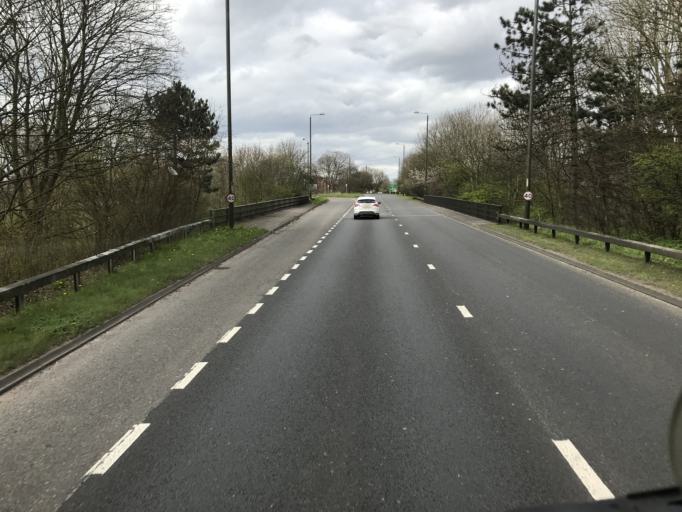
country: GB
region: England
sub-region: Derby
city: Derby
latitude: 52.9235
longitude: -1.5124
